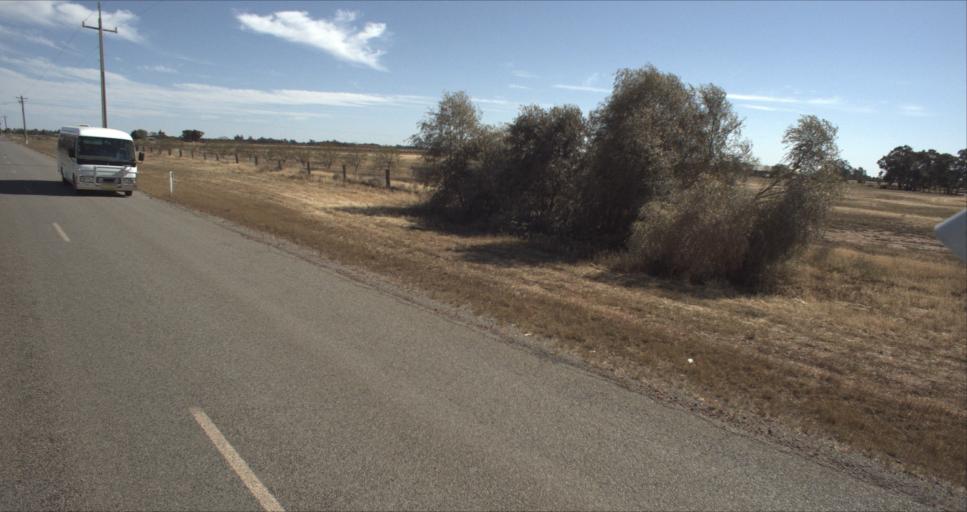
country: AU
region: New South Wales
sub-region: Leeton
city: Leeton
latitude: -34.5702
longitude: 146.3818
